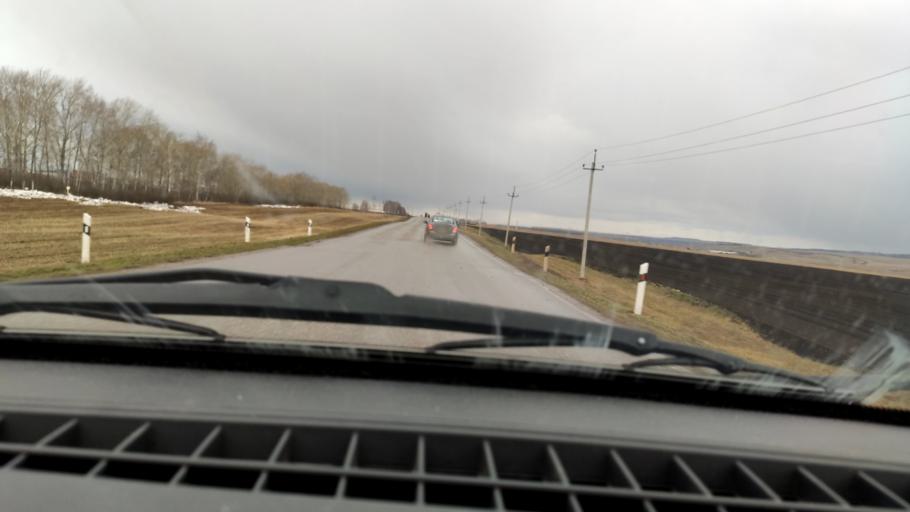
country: RU
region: Bashkortostan
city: Chekmagush
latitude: 55.1142
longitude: 54.8729
